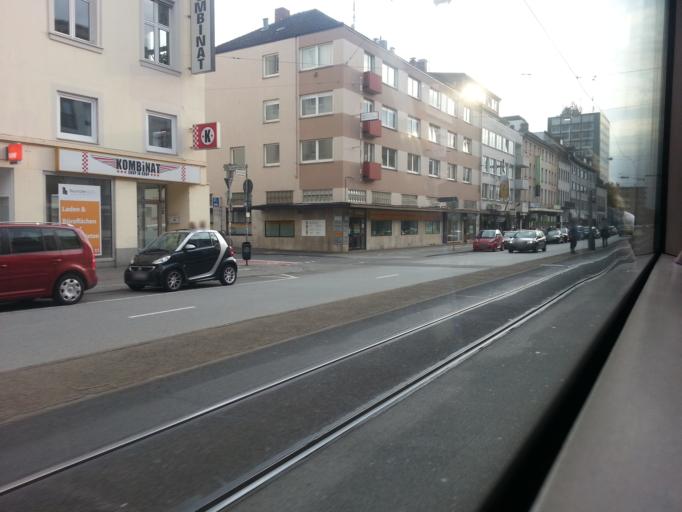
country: DE
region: Hesse
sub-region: Regierungsbezirk Darmstadt
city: Darmstadt
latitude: 49.8724
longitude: 8.6473
